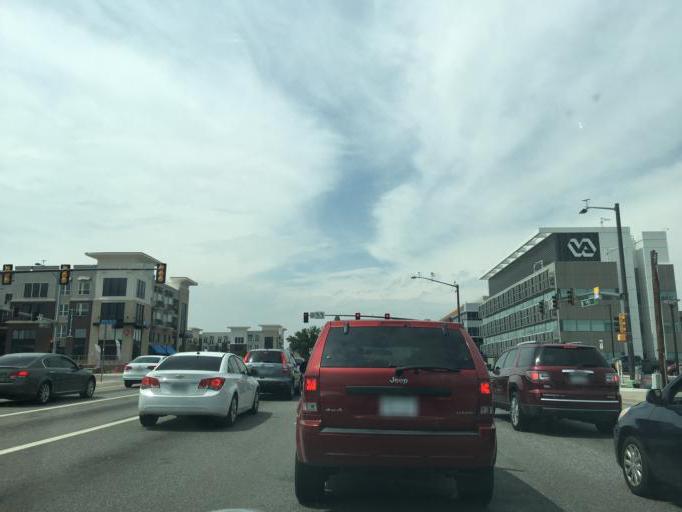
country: US
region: Colorado
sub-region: Adams County
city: Aurora
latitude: 39.7403
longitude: -104.8276
